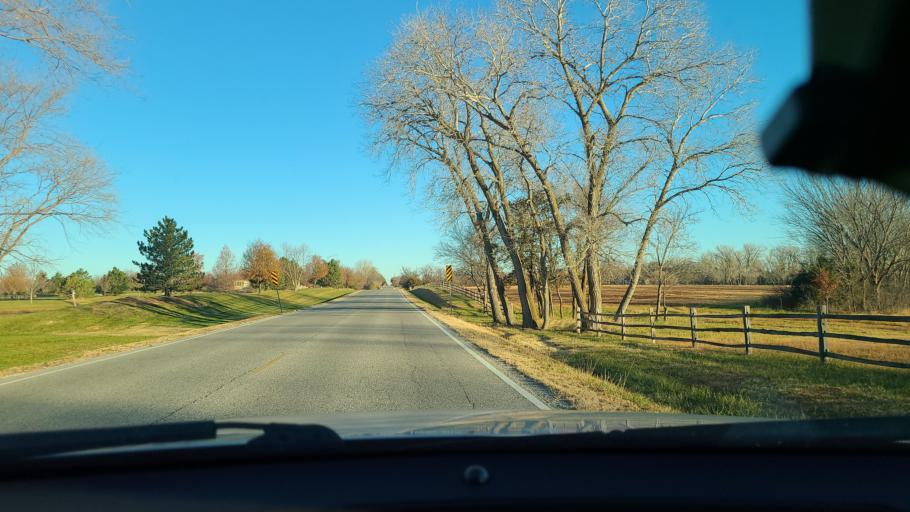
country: US
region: Kansas
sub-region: Sedgwick County
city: Park City
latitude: 37.8432
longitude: -97.3174
